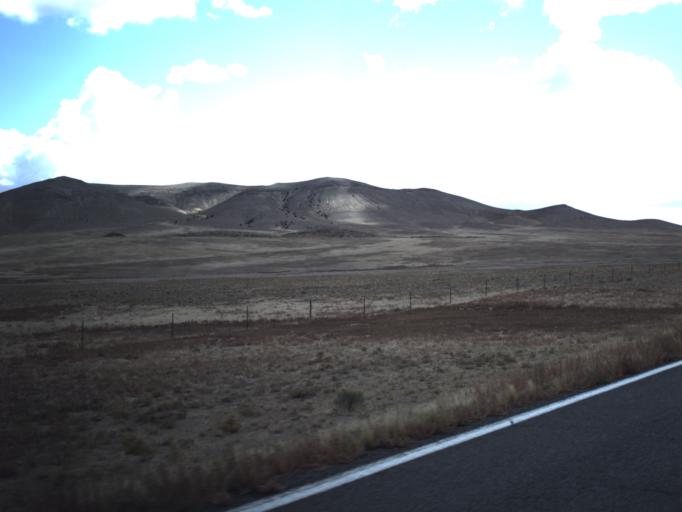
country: US
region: Utah
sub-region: Beaver County
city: Milford
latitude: 38.6435
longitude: -113.8638
